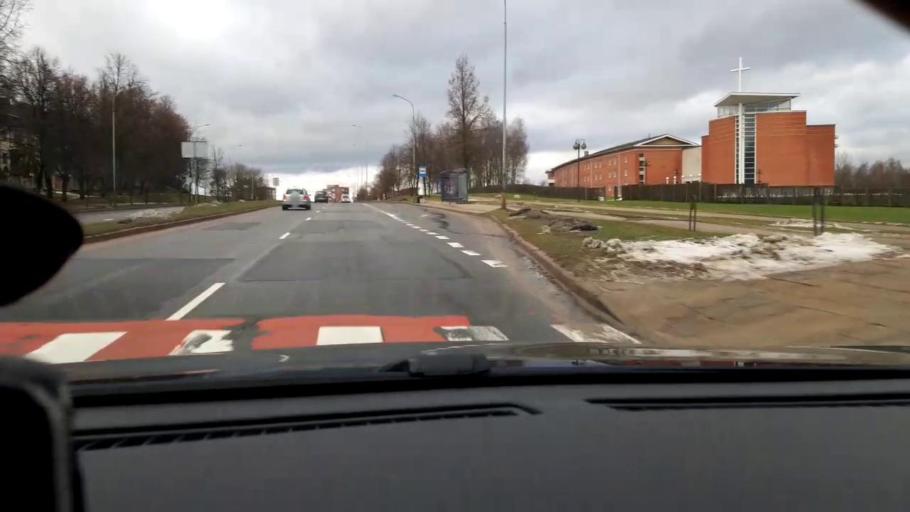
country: LT
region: Vilnius County
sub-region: Vilnius
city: Fabijoniskes
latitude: 54.7364
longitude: 25.2781
